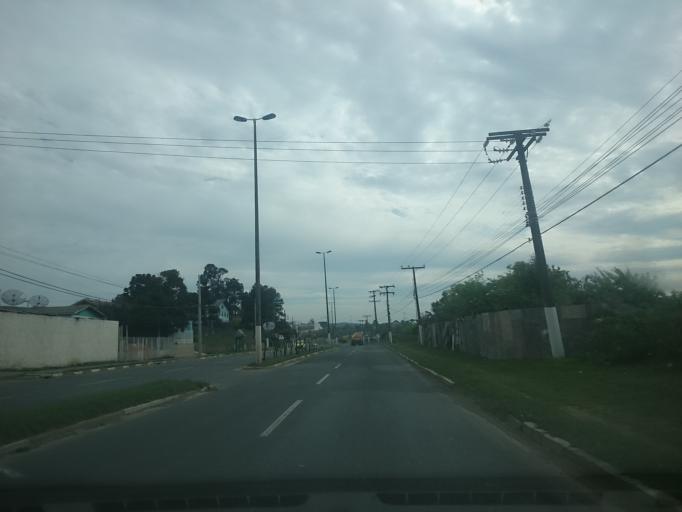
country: BR
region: Santa Catarina
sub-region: Lages
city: Lages
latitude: -27.7856
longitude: -50.3082
